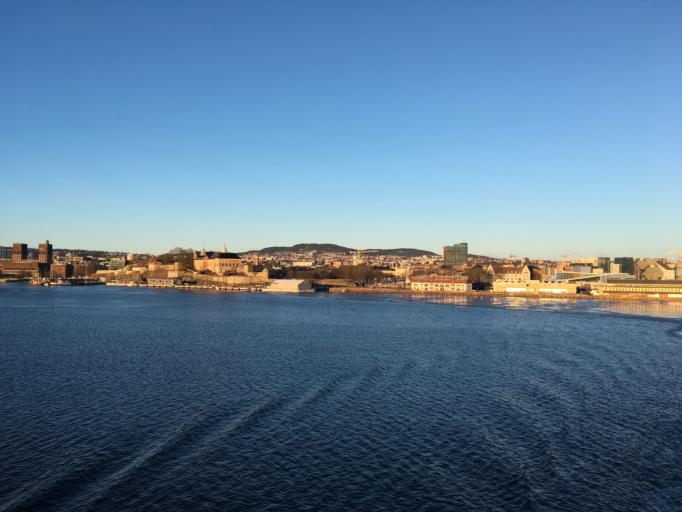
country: NO
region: Oslo
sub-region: Oslo
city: Oslo
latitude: 59.9003
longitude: 10.7310
